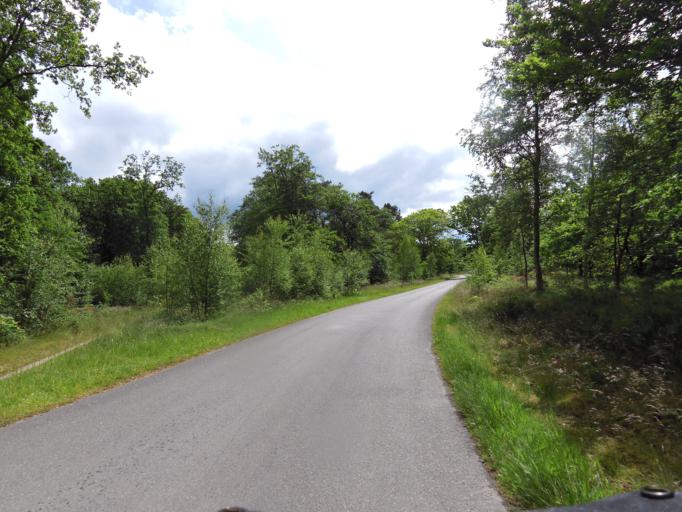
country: NL
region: Gelderland
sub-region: Gemeente Epe
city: Vaassen
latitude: 52.3093
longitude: 5.8936
